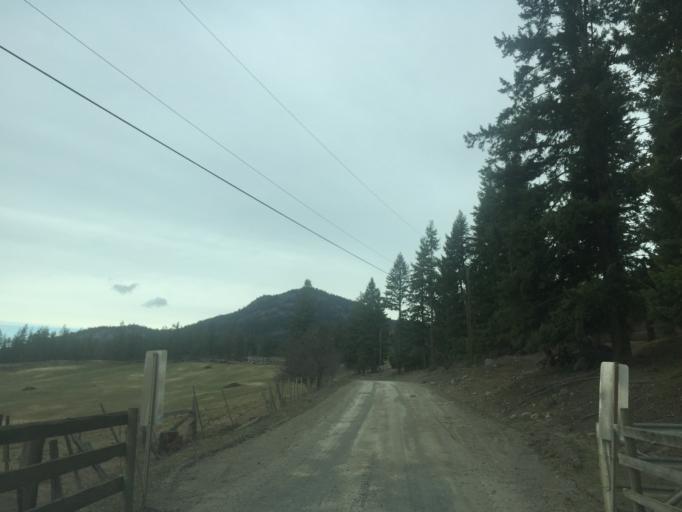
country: CA
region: British Columbia
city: Kamloops
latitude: 51.3560
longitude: -120.1591
